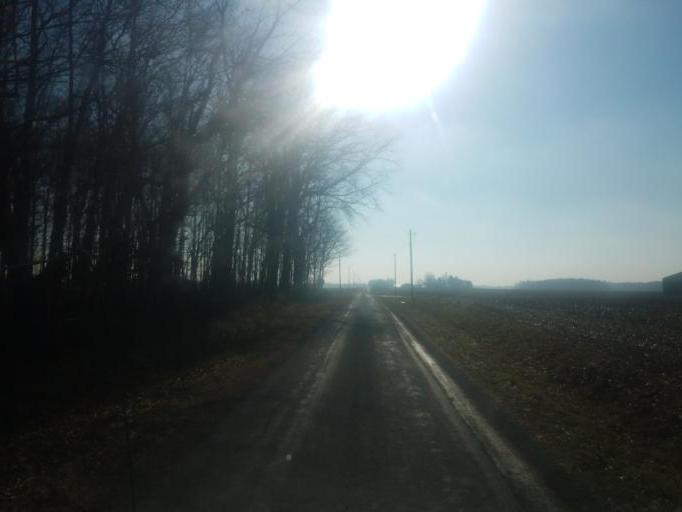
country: US
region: Ohio
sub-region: Crawford County
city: Bucyrus
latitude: 40.9564
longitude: -83.0742
